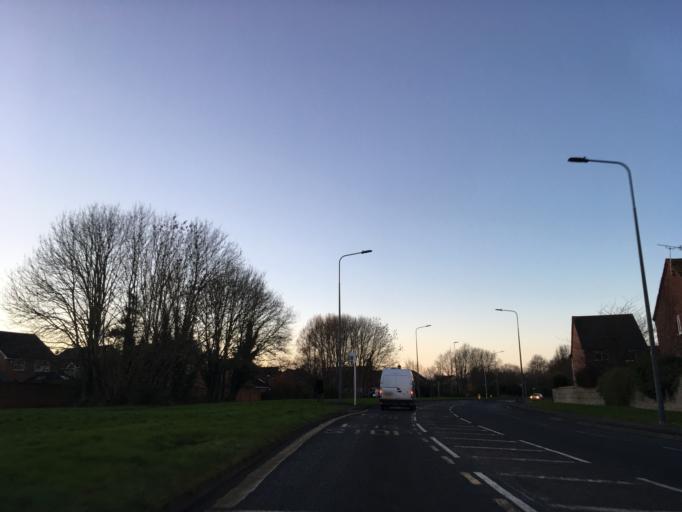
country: GB
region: England
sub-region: South Gloucestershire
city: Almondsbury
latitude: 51.5377
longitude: -2.5582
